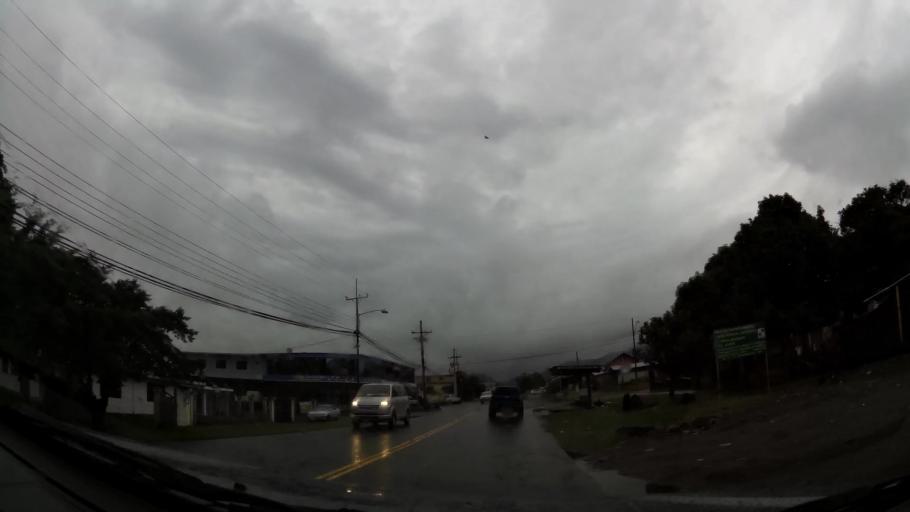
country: PA
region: Chiriqui
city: Volcan
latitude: 8.7774
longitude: -82.6430
